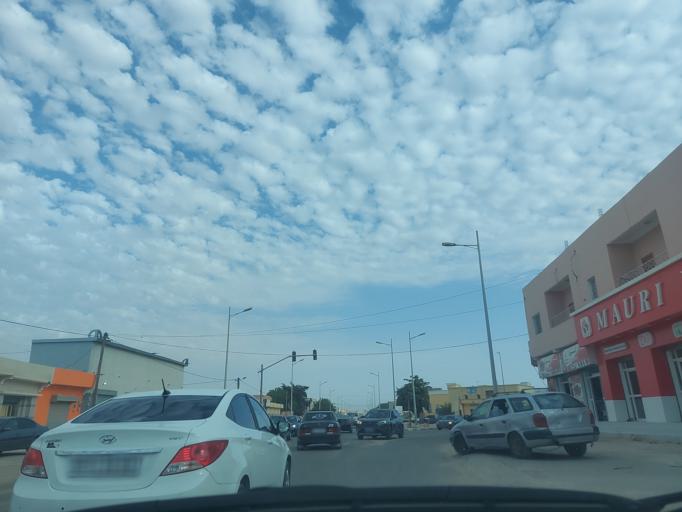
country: MR
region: Nouakchott
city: Nouakchott
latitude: 18.1178
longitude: -15.9750
